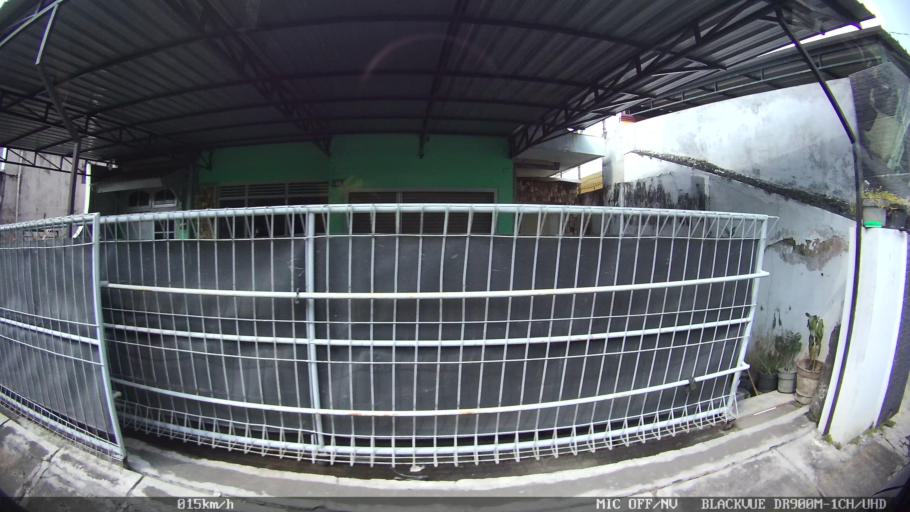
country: ID
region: Daerah Istimewa Yogyakarta
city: Yogyakarta
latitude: -7.8120
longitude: 110.3781
